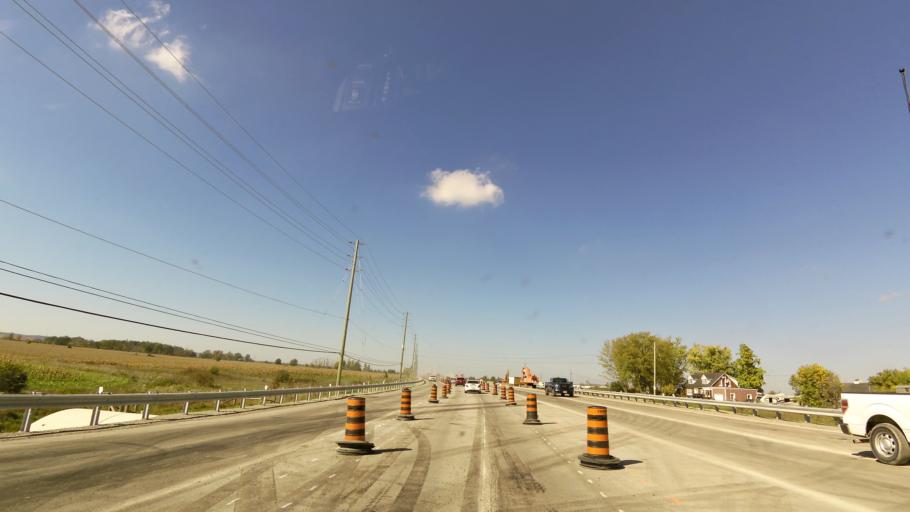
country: CA
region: Ontario
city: Burlington
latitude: 43.4680
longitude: -79.8093
